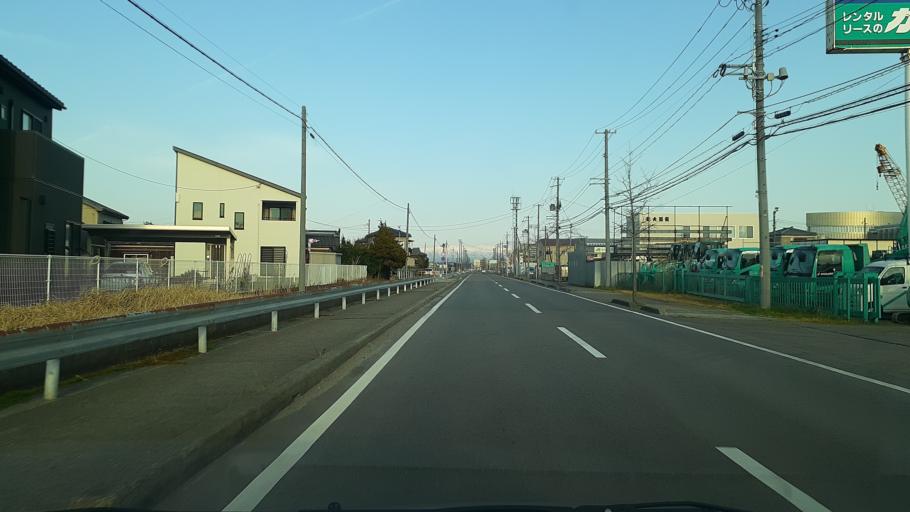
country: JP
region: Niigata
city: Niigata-shi
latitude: 37.8676
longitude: 139.0280
